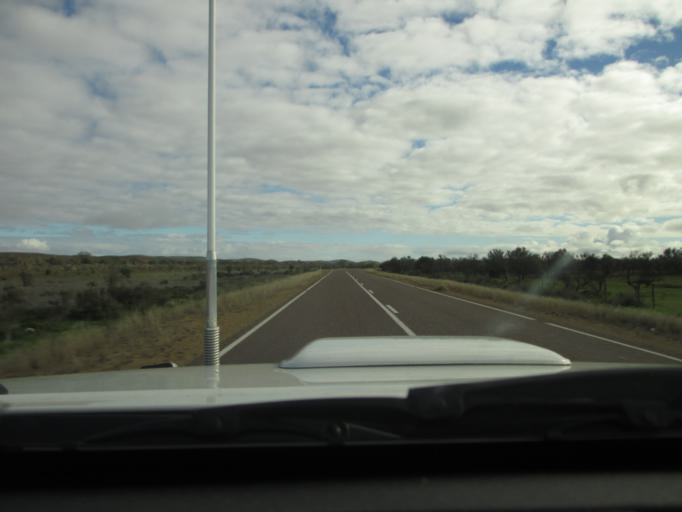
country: AU
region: South Australia
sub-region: Flinders Ranges
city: Quorn
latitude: -32.3554
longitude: 138.4913
